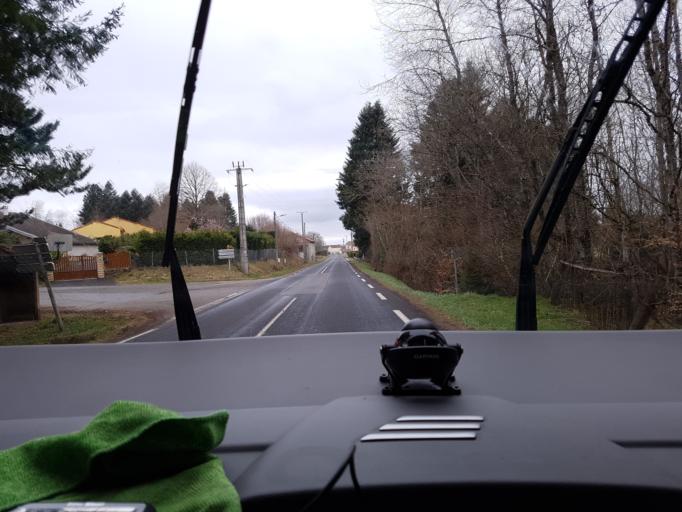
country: FR
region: Auvergne
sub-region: Departement du Puy-de-Dome
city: Saint-Ours
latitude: 45.8588
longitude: 2.9235
